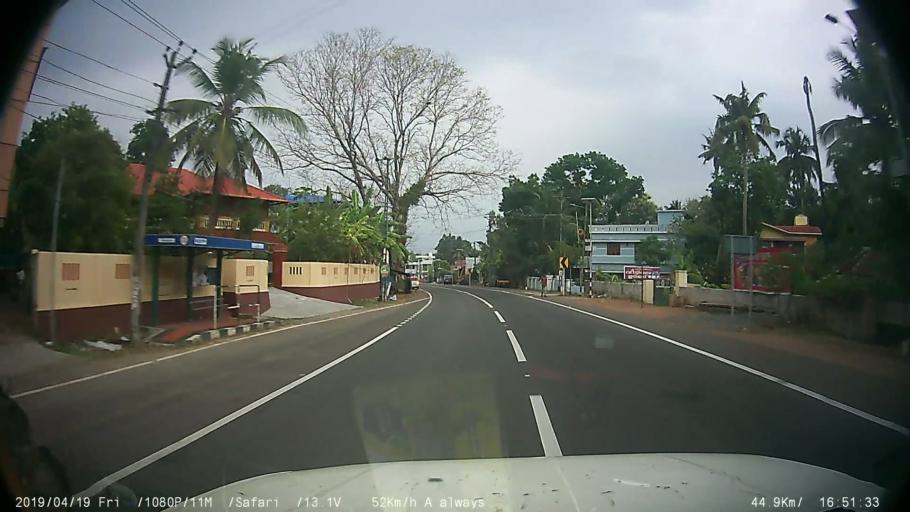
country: IN
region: Kerala
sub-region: Kottayam
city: Changanacheri
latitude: 9.4565
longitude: 76.5338
